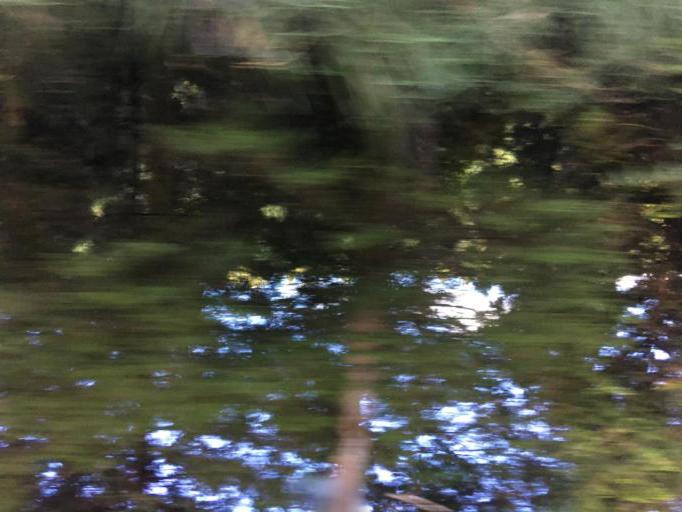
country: TW
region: Taiwan
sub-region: Yilan
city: Yilan
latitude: 24.5115
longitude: 121.5925
